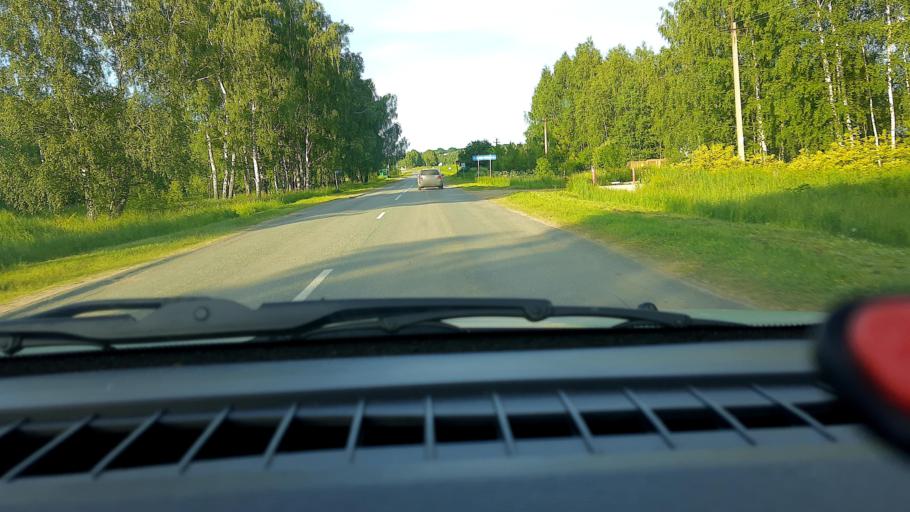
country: RU
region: Nizjnij Novgorod
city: Afonino
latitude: 56.1213
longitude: 43.9988
